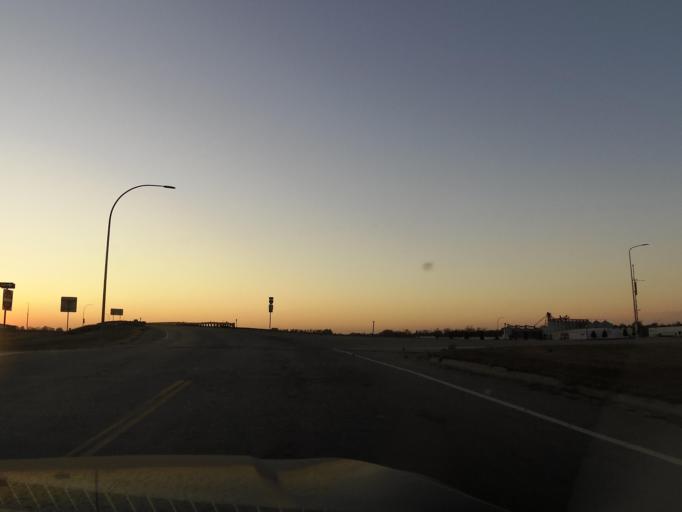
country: US
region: North Dakota
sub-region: Traill County
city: Hillsboro
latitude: 47.4032
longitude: -97.0725
